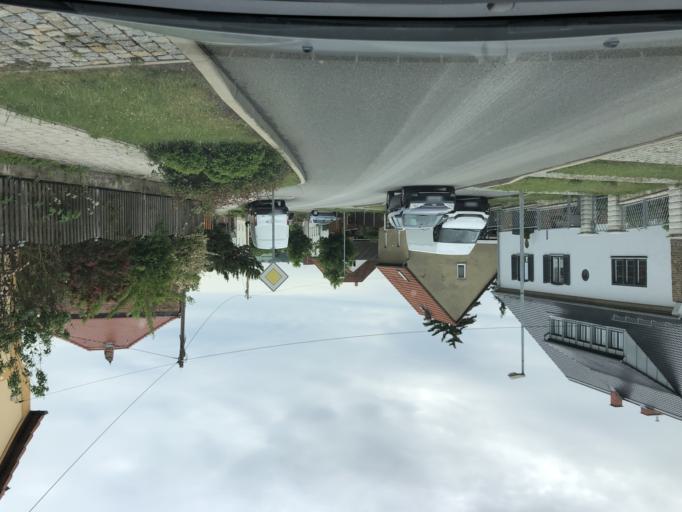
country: DE
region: Thuringia
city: Ossmanstedt
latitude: 51.0214
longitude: 11.4255
